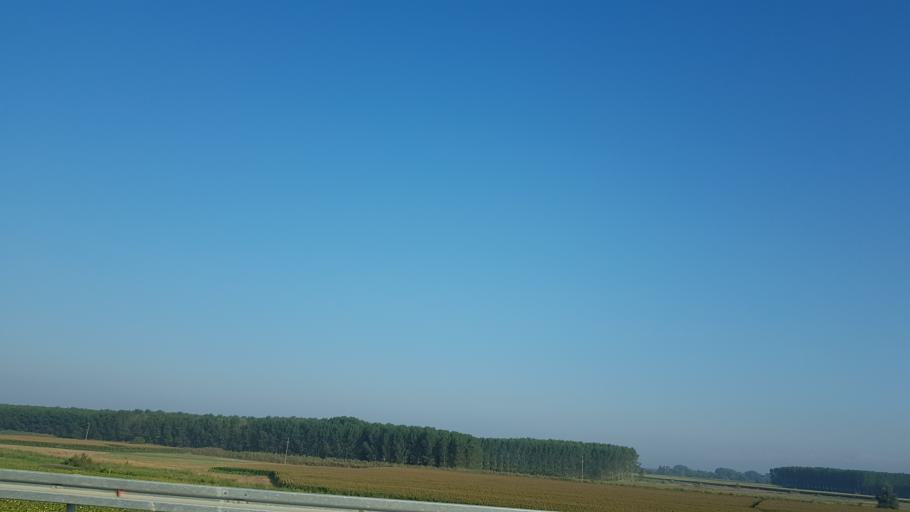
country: TR
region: Bursa
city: Karacabey
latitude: 40.1445
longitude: 28.3053
